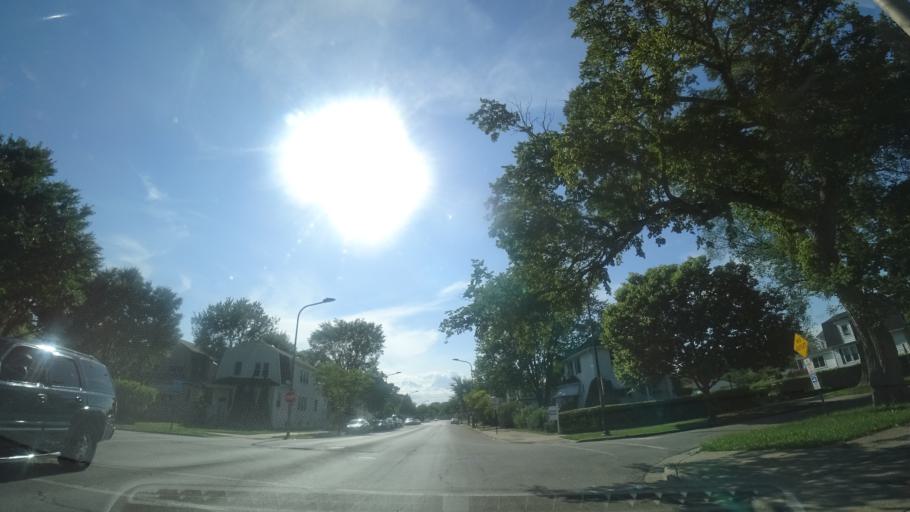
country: US
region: Illinois
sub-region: Cook County
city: Evanston
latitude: 42.0557
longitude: -87.6971
